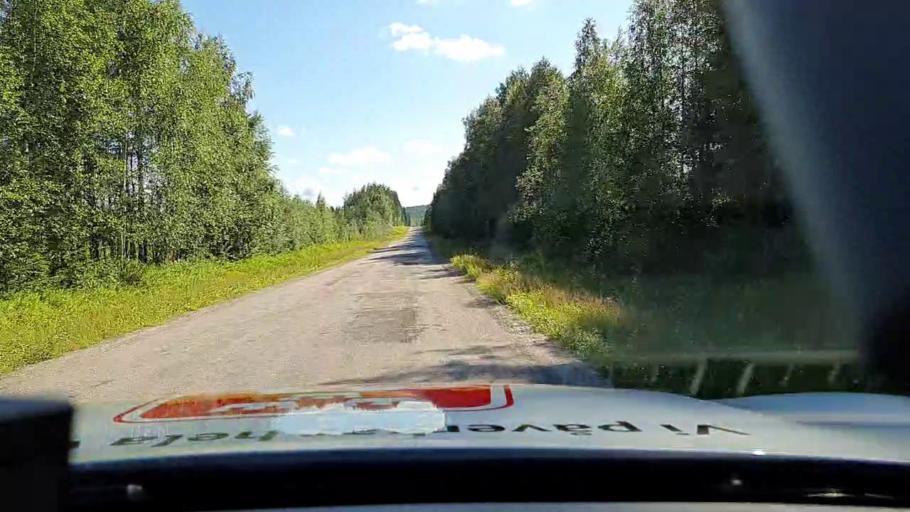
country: SE
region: Norrbotten
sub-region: Overkalix Kommun
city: OEverkalix
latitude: 66.2567
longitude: 23.0211
